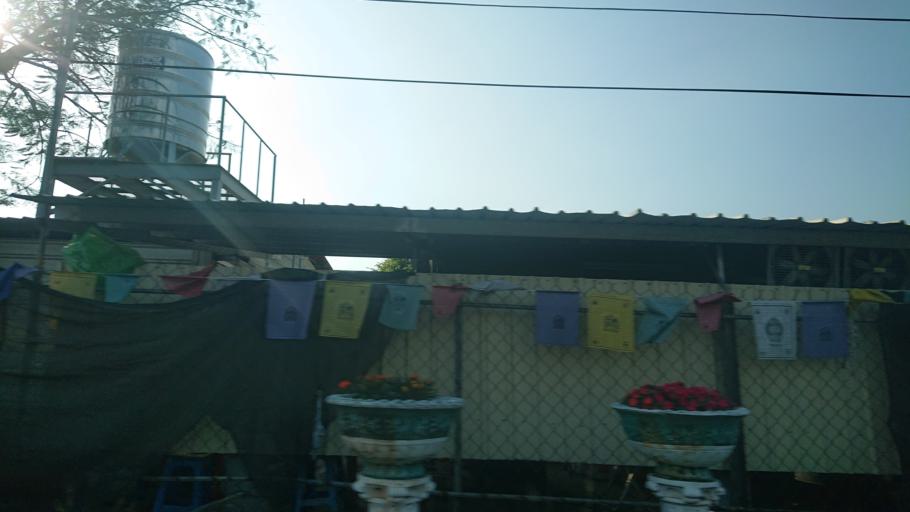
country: TW
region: Taiwan
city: Xinying
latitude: 23.1555
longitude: 120.2495
